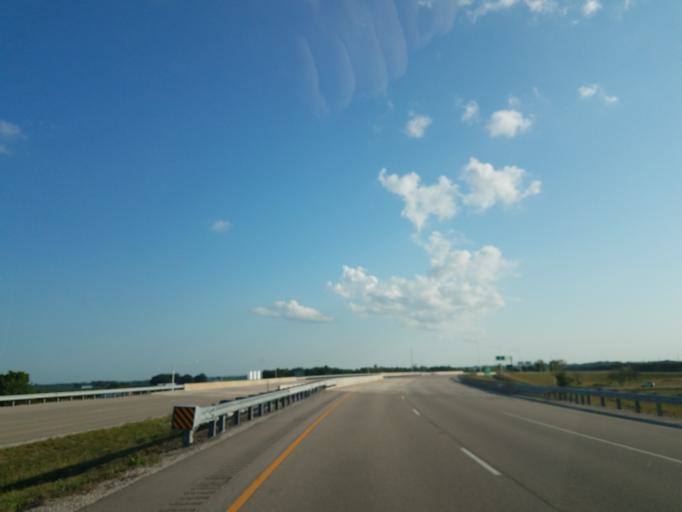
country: US
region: Illinois
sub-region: McLean County
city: Bloomington
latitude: 40.4425
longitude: -89.0174
